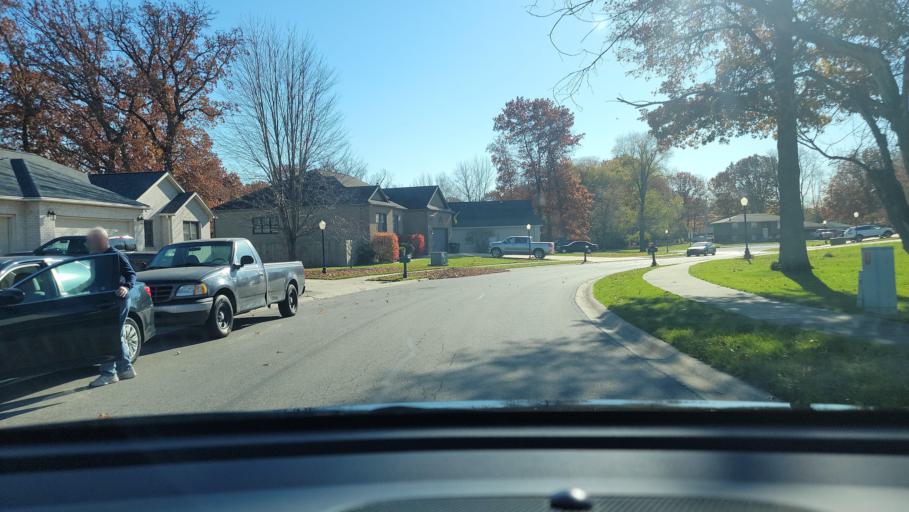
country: US
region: Indiana
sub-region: Porter County
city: Portage
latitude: 41.5877
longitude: -87.1472
